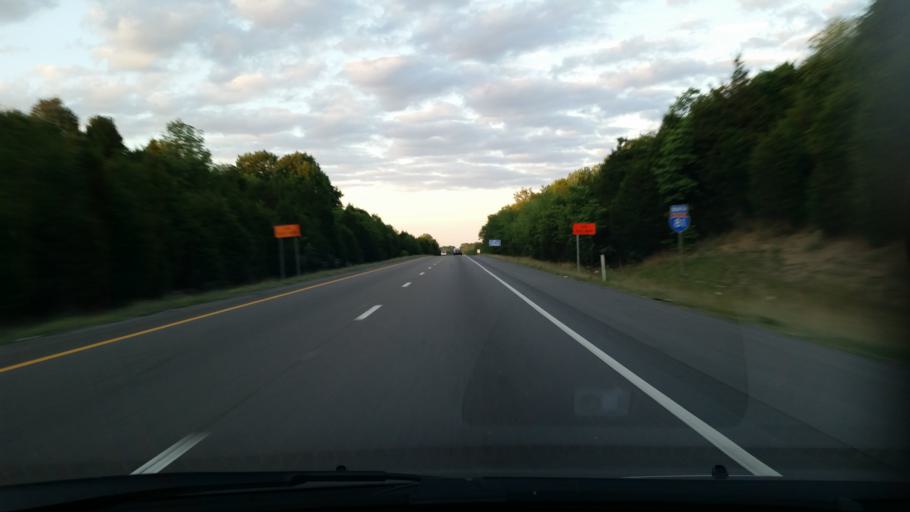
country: US
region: Tennessee
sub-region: Greene County
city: Mosheim
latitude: 36.2276
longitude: -83.0298
